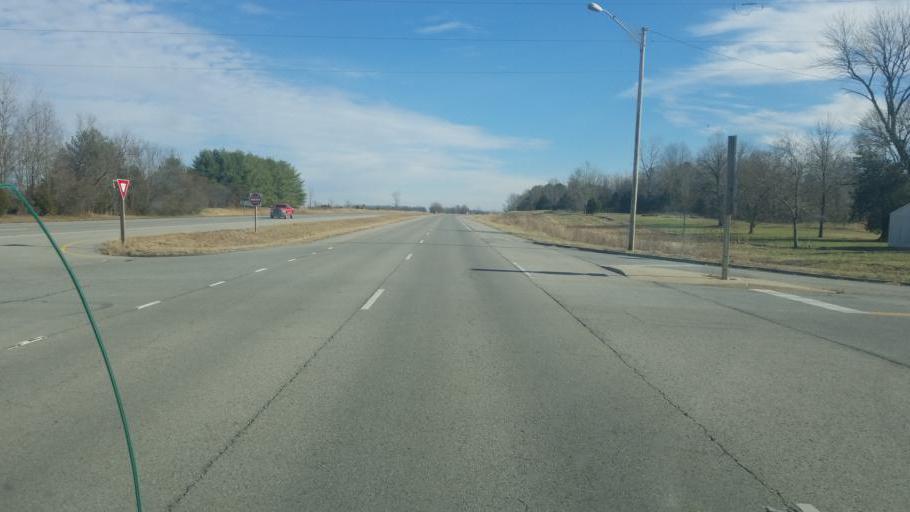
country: US
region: Illinois
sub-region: Williamson County
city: Marion
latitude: 37.7326
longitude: -88.7993
